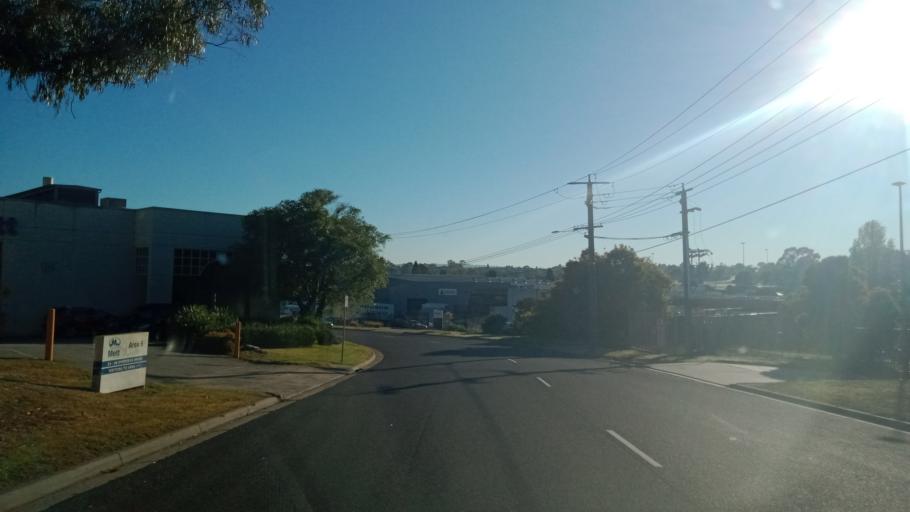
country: AU
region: Victoria
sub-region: Greater Dandenong
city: Noble Park North
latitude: -37.9545
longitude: 145.1875
